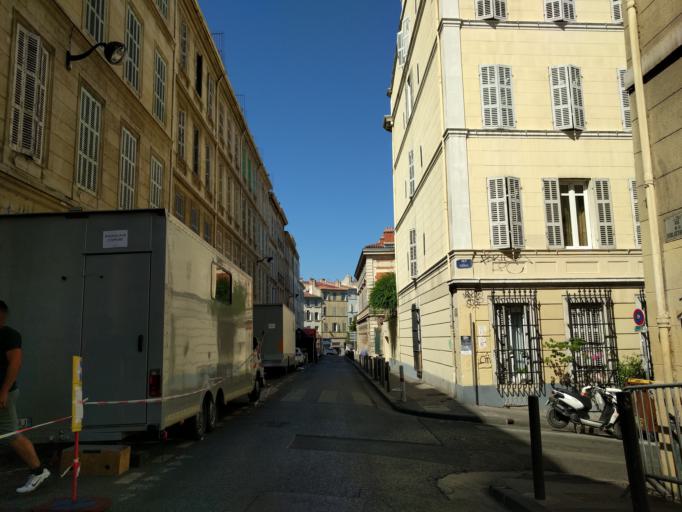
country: FR
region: Provence-Alpes-Cote d'Azur
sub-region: Departement des Bouches-du-Rhone
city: Marseille 01
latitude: 43.2956
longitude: 5.3849
